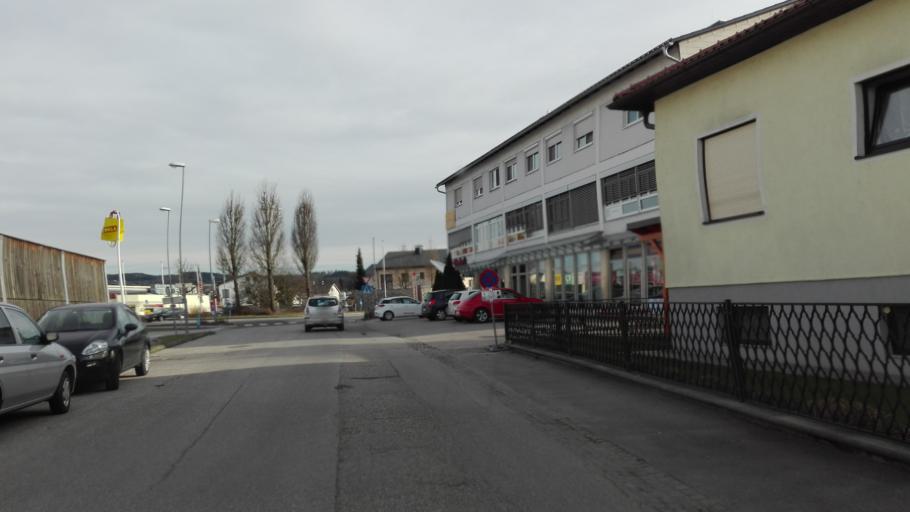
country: AT
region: Upper Austria
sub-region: Politischer Bezirk Urfahr-Umgebung
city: Ottensheim
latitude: 48.3404
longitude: 14.1669
